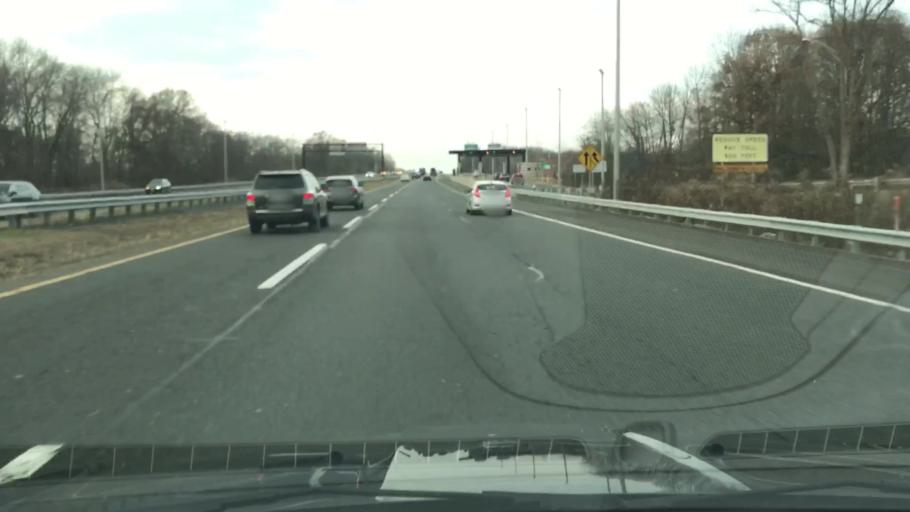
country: US
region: New Jersey
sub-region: Burlington County
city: Roebling
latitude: 40.1003
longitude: -74.7875
